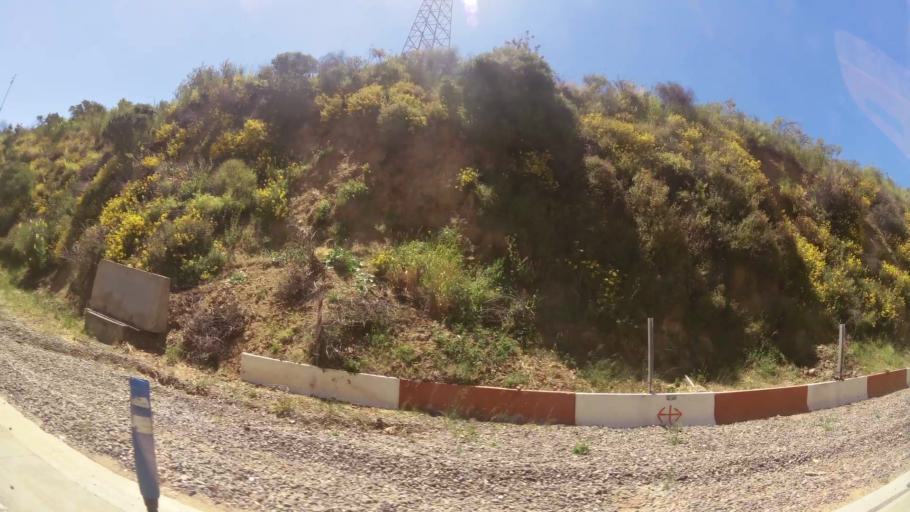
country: CL
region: Valparaiso
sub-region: Provincia de Valparaiso
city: Valparaiso
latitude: -33.0588
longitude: -71.6511
